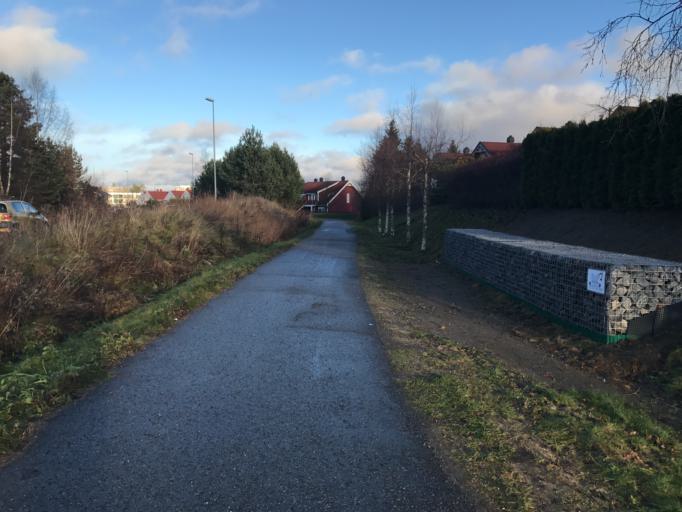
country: NO
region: Akershus
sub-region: Ullensaker
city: Jessheim
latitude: 60.1385
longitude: 11.1898
